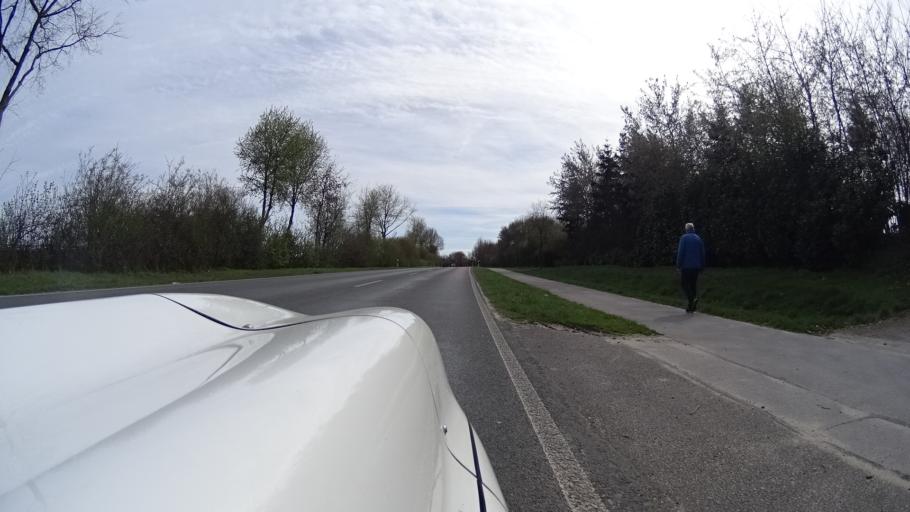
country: DE
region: North Rhine-Westphalia
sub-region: Regierungsbezirk Dusseldorf
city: Kevelaer
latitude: 51.5594
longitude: 6.2032
